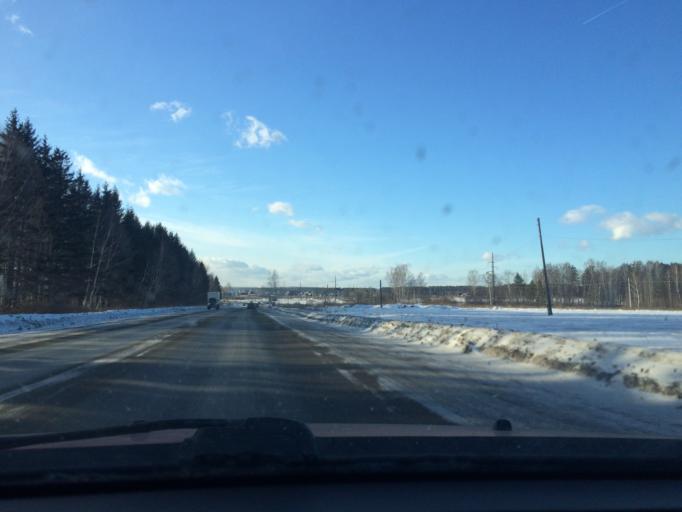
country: RU
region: Sverdlovsk
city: Aramil
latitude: 56.7722
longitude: 60.8614
